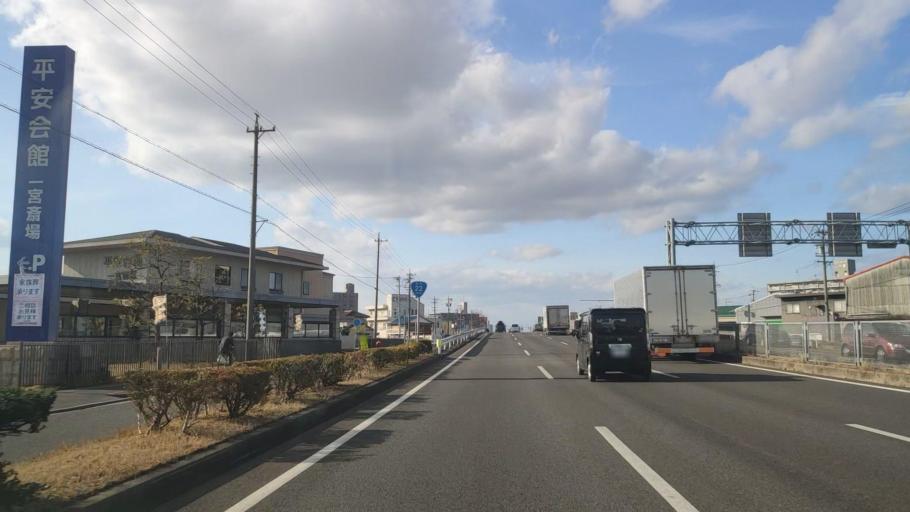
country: JP
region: Aichi
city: Ichinomiya
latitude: 35.3150
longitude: 136.8152
